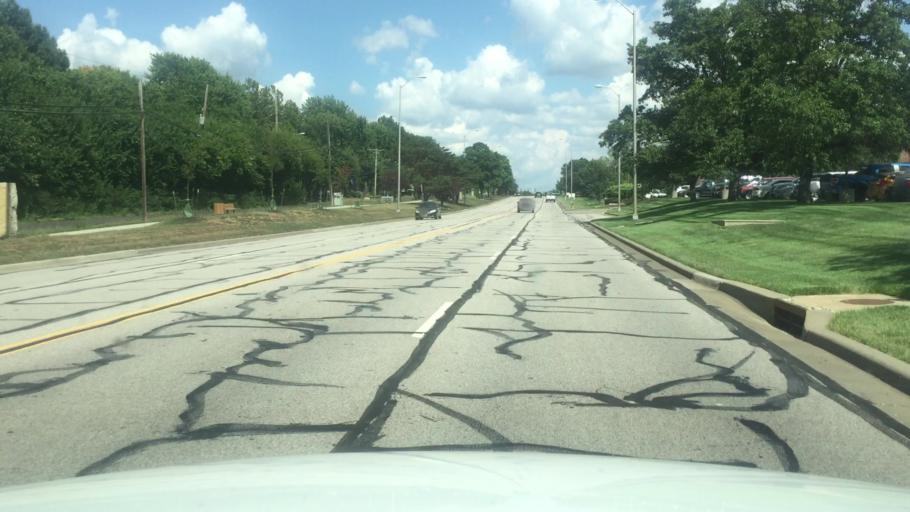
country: US
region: Kansas
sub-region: Johnson County
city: Lenexa
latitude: 38.9562
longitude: -94.7529
